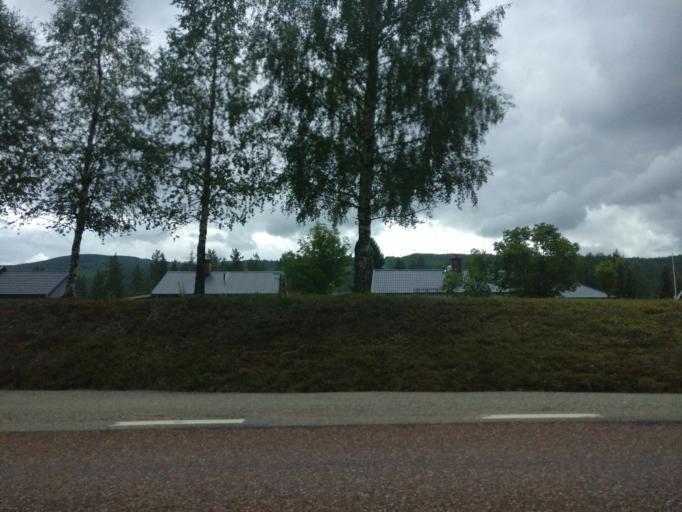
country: SE
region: Vaermland
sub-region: Torsby Kommun
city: Torsby
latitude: 60.7519
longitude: 12.7870
